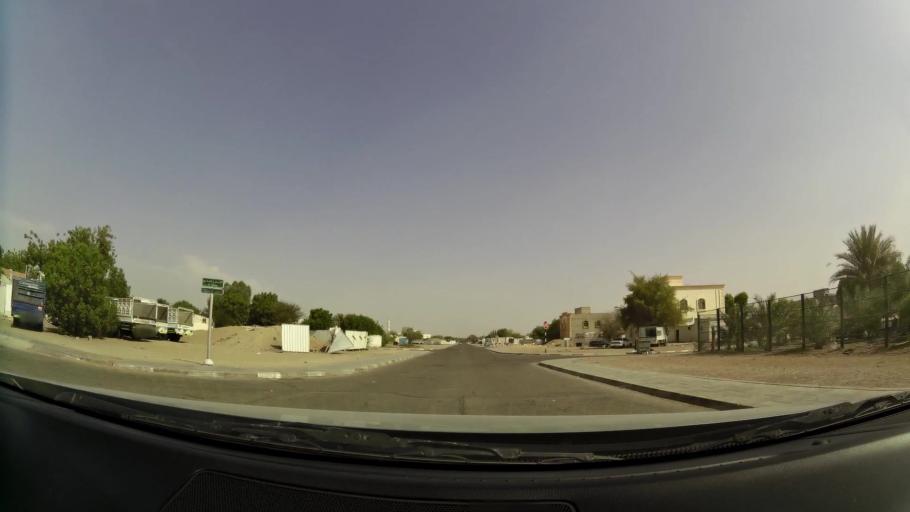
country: AE
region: Abu Dhabi
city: Al Ain
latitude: 24.2408
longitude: 55.7007
